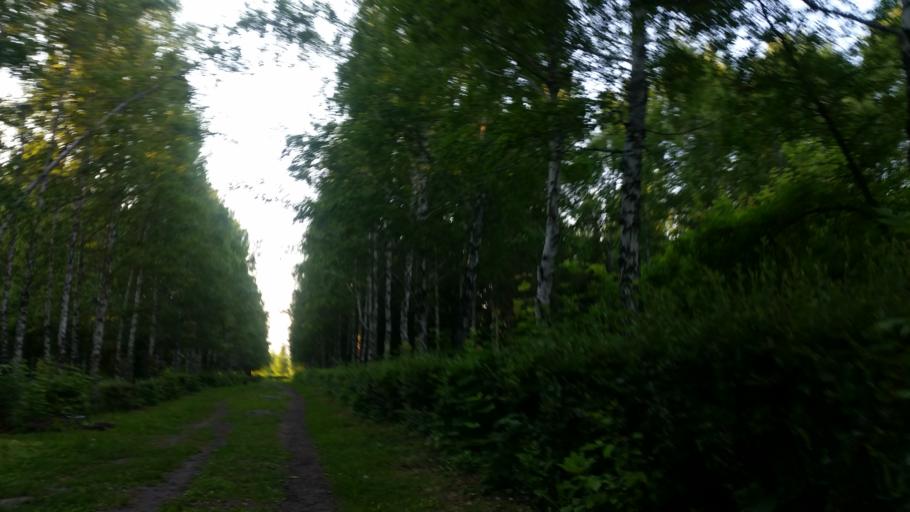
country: RU
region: Ulyanovsk
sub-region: Ulyanovskiy Rayon
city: Ulyanovsk
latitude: 54.3478
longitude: 48.3942
